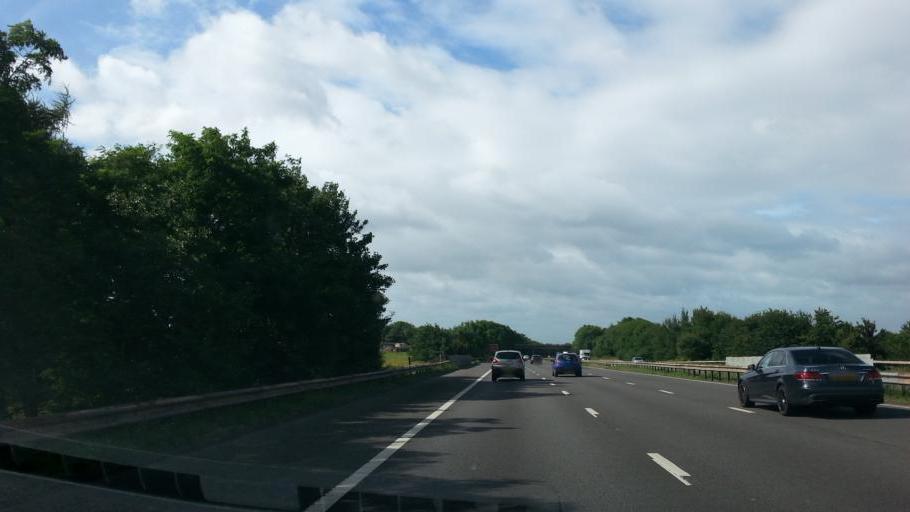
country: GB
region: England
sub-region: Warwickshire
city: Bedworth
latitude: 52.4602
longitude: -1.4139
